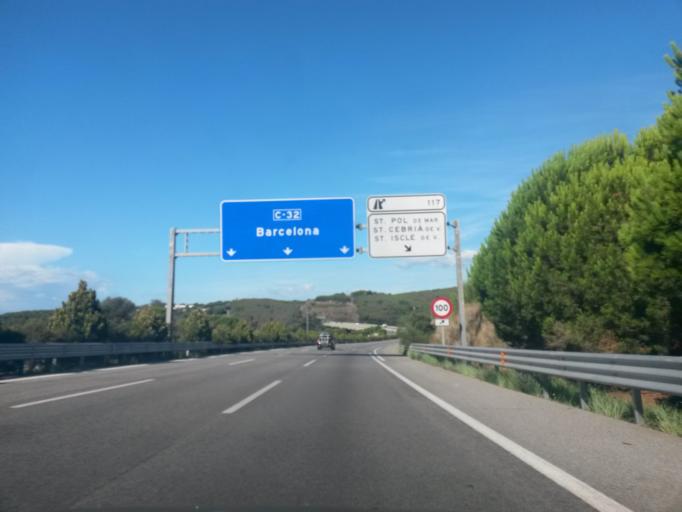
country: ES
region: Catalonia
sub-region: Provincia de Barcelona
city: Sant Pol de Mar
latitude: 41.6063
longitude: 2.6137
